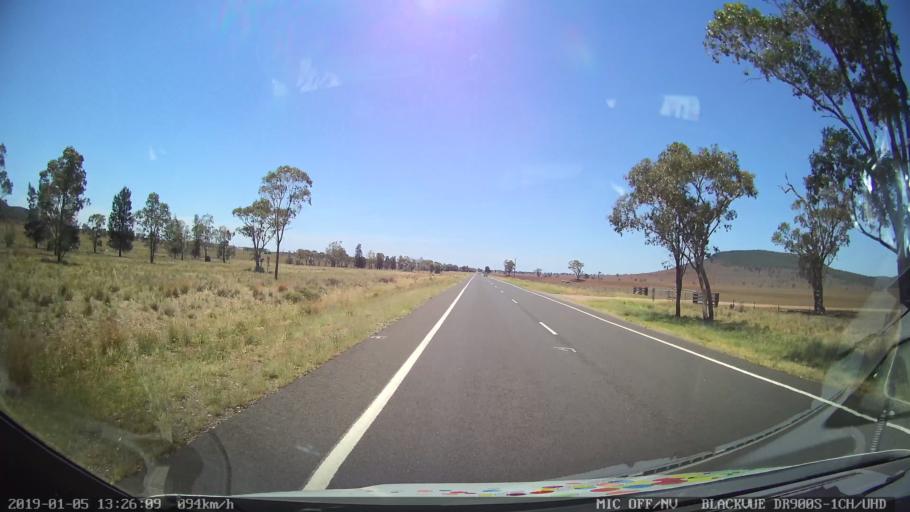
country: AU
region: New South Wales
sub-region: Gunnedah
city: Gunnedah
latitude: -31.0554
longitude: 150.0116
